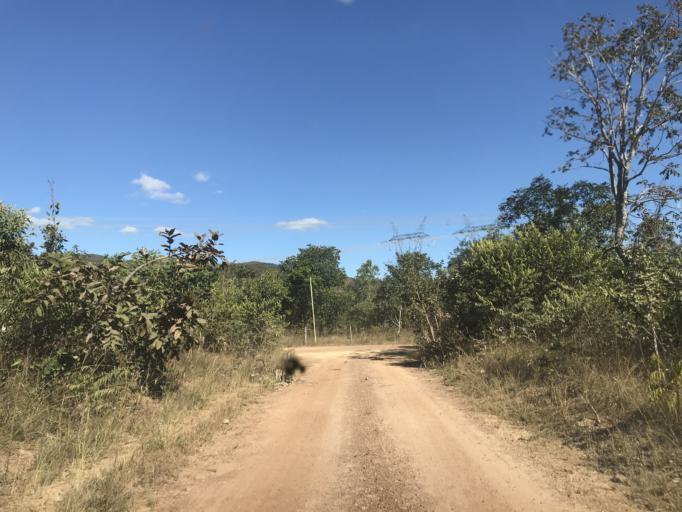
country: BR
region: Goias
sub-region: Padre Bernardo
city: Padre Bernardo
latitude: -15.4093
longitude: -48.2273
